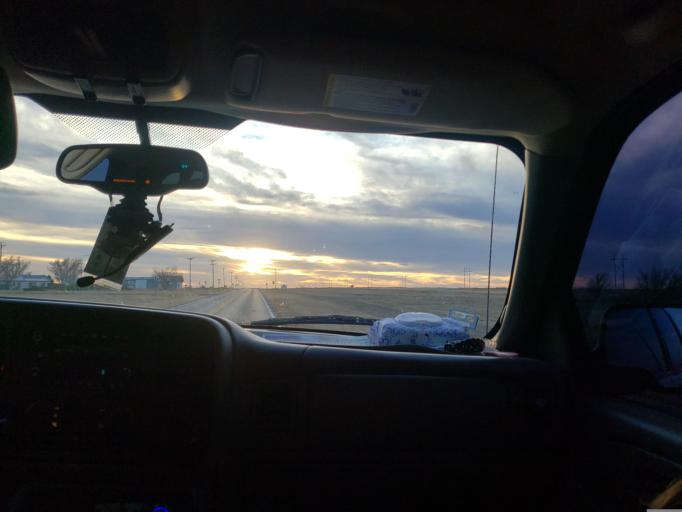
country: US
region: Oklahoma
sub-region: Cimarron County
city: Boise City
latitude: 36.8089
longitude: -102.2566
